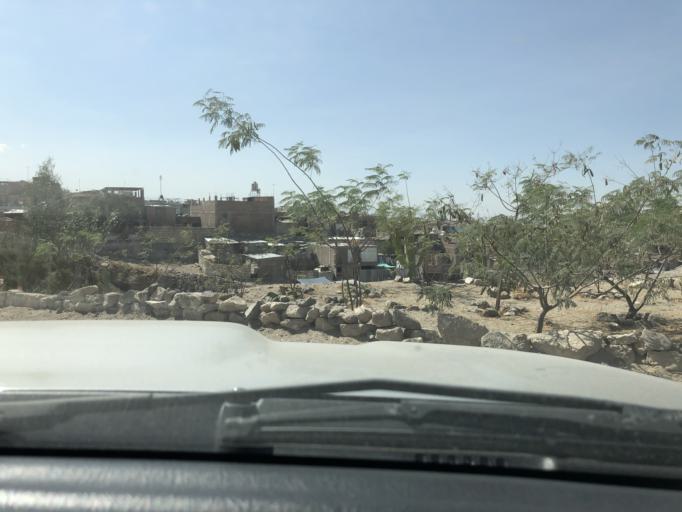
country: PE
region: Arequipa
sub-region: Provincia de Arequipa
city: Arequipa
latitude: -16.3431
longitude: -71.5507
